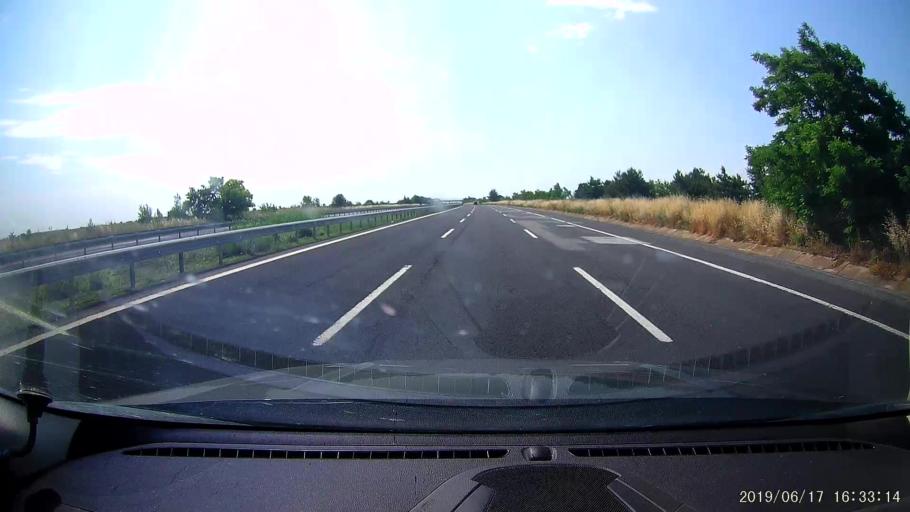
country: TR
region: Kirklareli
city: Buyukkaristiran
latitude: 41.3794
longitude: 27.5793
